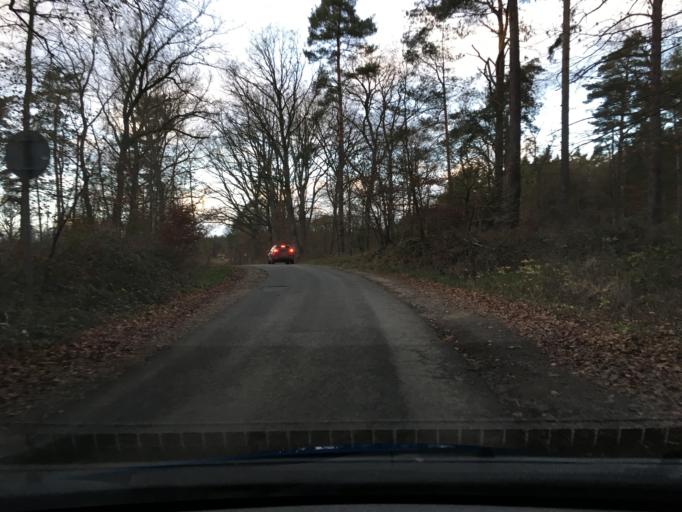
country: DE
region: Lower Saxony
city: Oldendorf
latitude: 53.1435
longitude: 10.1971
